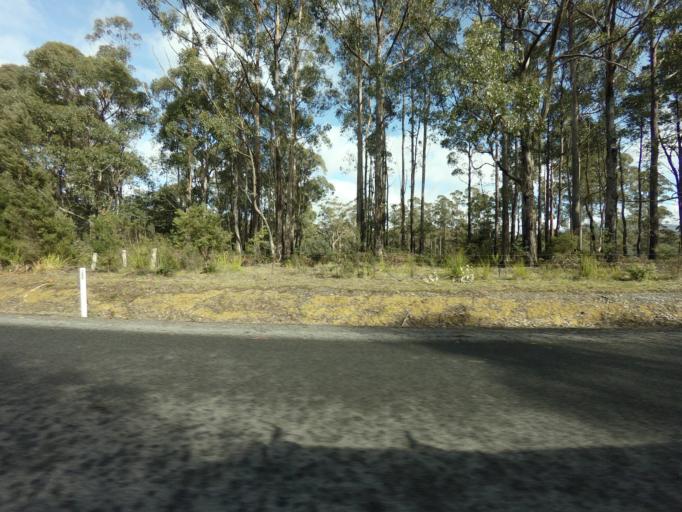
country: AU
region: Tasmania
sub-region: Huon Valley
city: Geeveston
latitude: -43.4195
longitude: 146.9076
